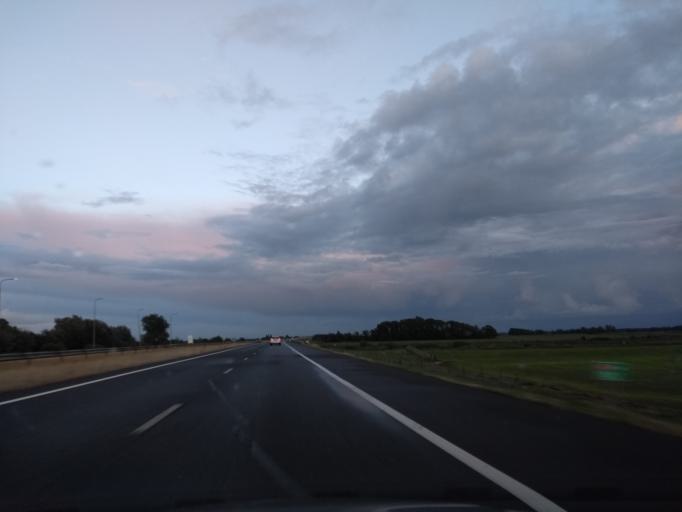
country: NL
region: Friesland
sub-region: Sudwest Fryslan
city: Oppenhuizen
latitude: 52.9839
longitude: 5.7346
